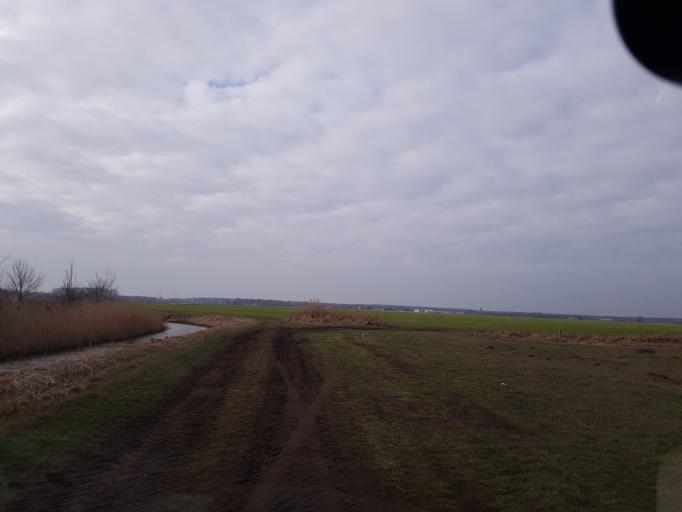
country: DE
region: Brandenburg
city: Doberlug-Kirchhain
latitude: 51.6638
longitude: 13.5666
